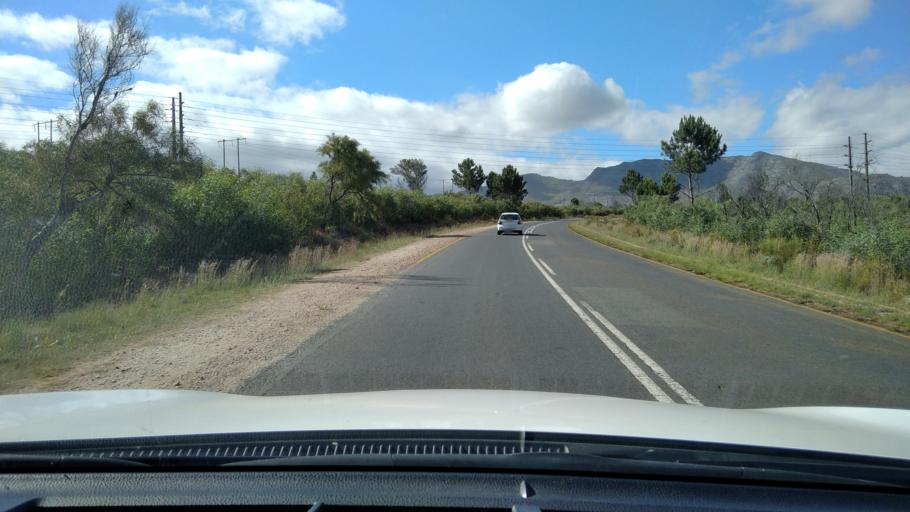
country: ZA
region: Western Cape
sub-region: Overberg District Municipality
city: Hermanus
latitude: -34.2436
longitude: 19.1850
